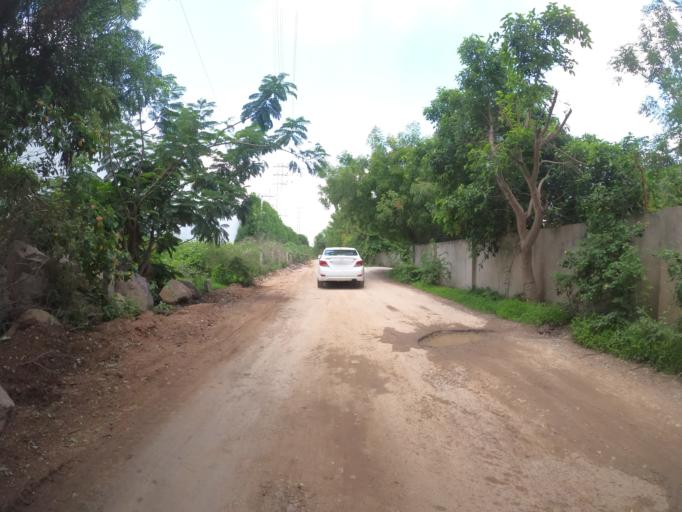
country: IN
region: Telangana
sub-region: Medak
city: Serilingampalle
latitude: 17.3746
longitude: 78.3221
